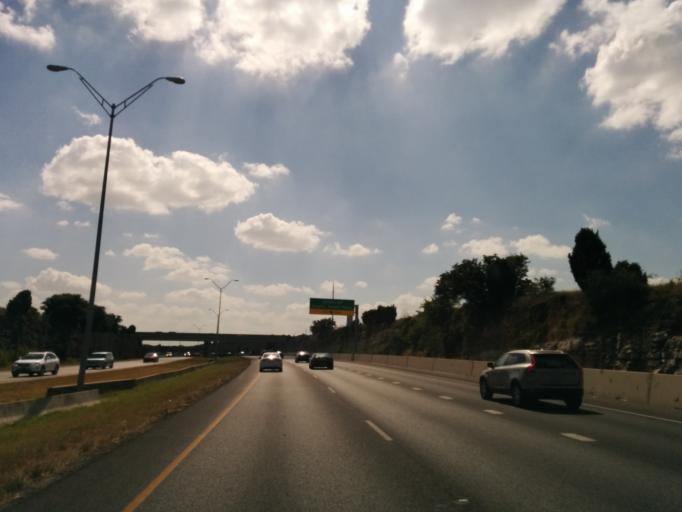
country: US
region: Texas
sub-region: Bexar County
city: Hollywood Park
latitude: 29.6087
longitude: -98.5204
